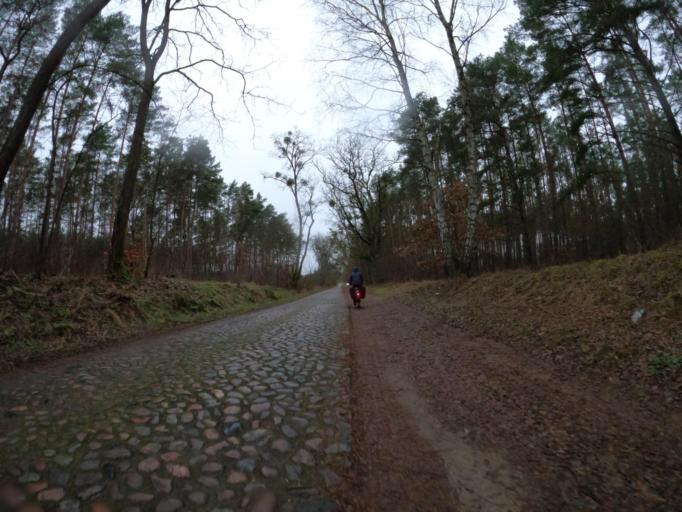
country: PL
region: West Pomeranian Voivodeship
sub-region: Powiat mysliborski
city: Debno
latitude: 52.8080
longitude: 14.7384
